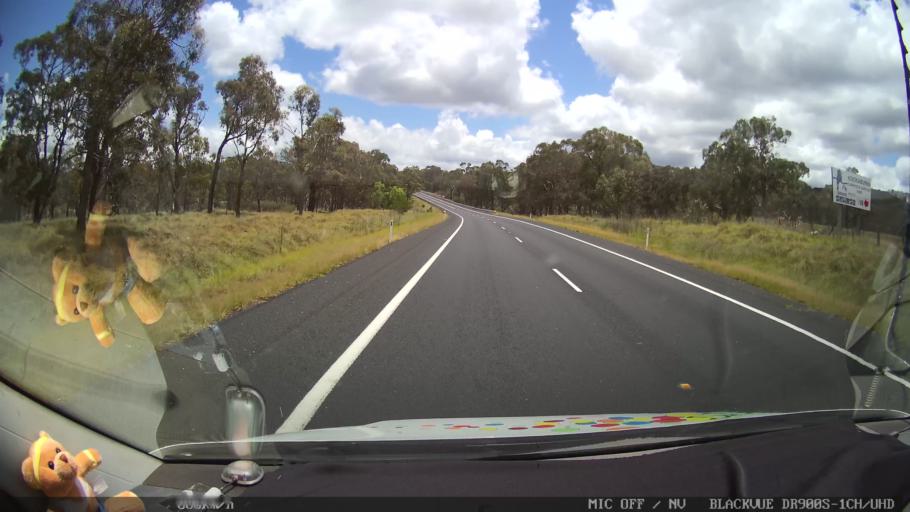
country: AU
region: New South Wales
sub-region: Glen Innes Severn
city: Glen Innes
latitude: -29.3618
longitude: 151.8988
